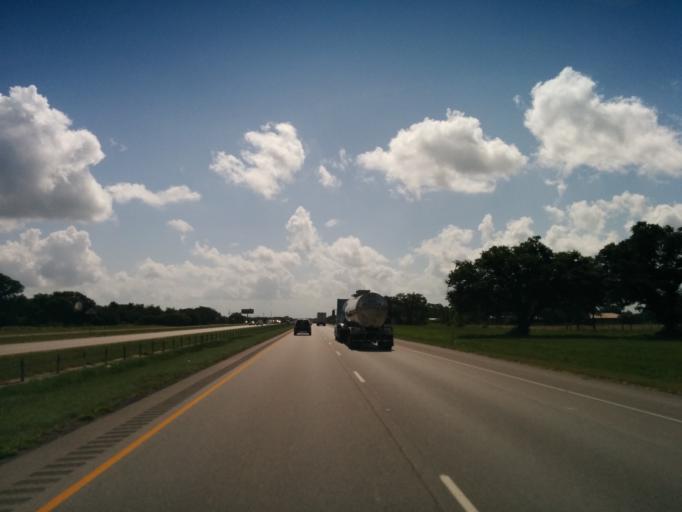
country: US
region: Texas
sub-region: Colorado County
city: Columbus
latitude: 29.6935
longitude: -96.5872
